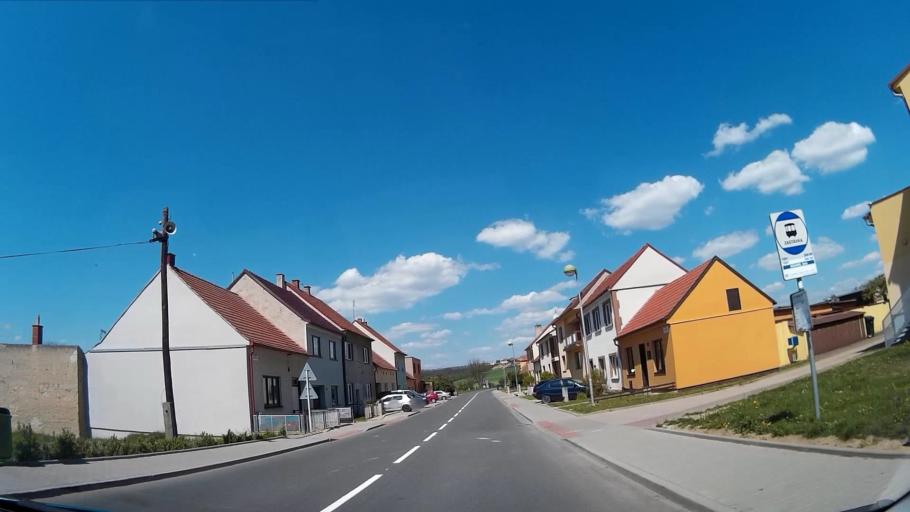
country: CZ
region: South Moravian
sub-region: Okres Brno-Venkov
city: Rosice
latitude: 49.1459
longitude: 16.3873
